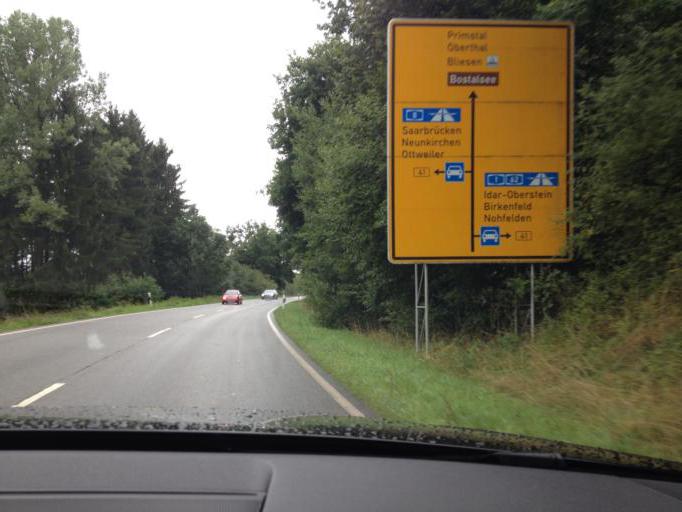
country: DE
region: Saarland
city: Sankt Wendel
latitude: 49.4801
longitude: 7.1507
